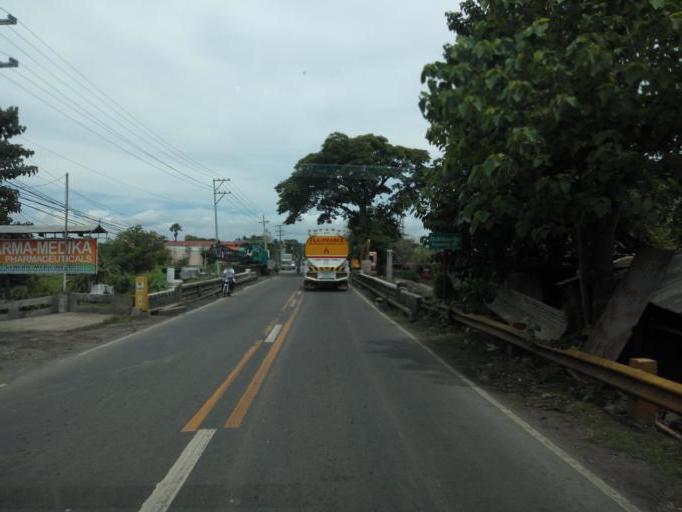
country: PH
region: Cagayan Valley
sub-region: Province of Isabela
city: Santiago
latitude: 16.6919
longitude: 121.5351
